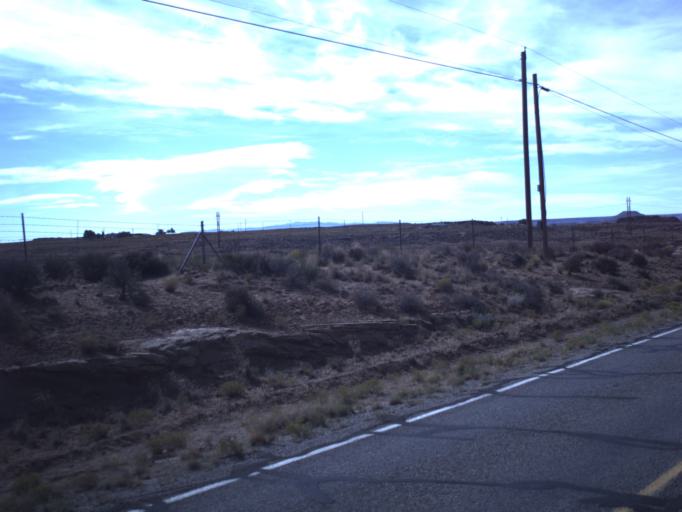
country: US
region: Utah
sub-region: San Juan County
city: Blanding
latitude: 37.2861
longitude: -109.2909
